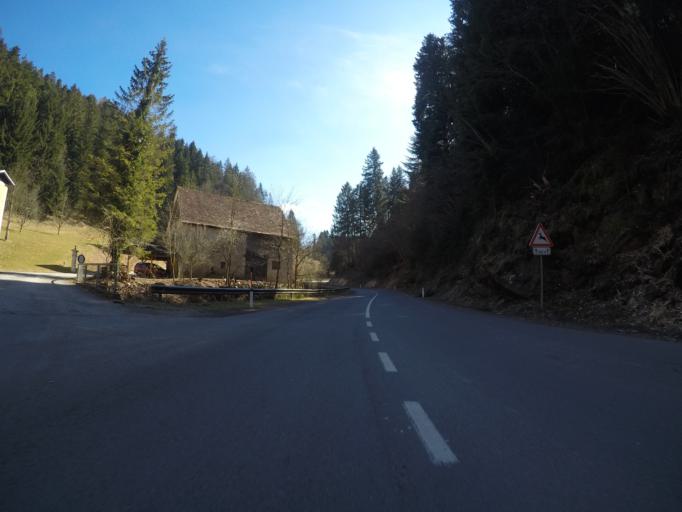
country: SI
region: Lovrenc na Pohorju
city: Lovrenc na Pohorju
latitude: 46.5518
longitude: 15.4229
